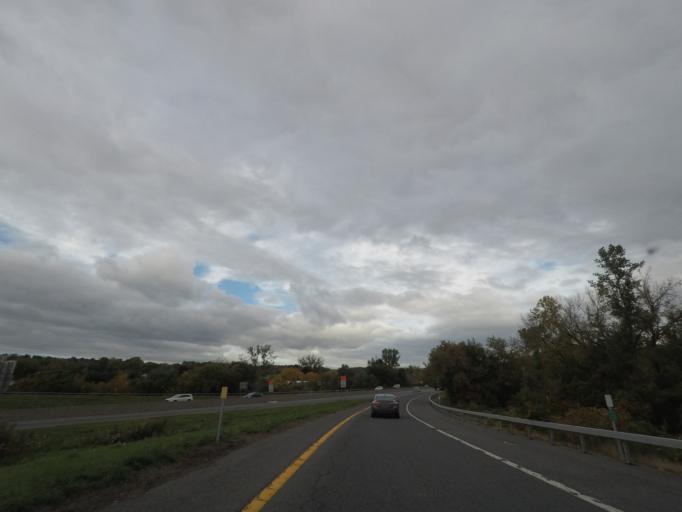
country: US
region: New York
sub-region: Albany County
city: Green Island
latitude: 42.7448
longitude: -73.6968
